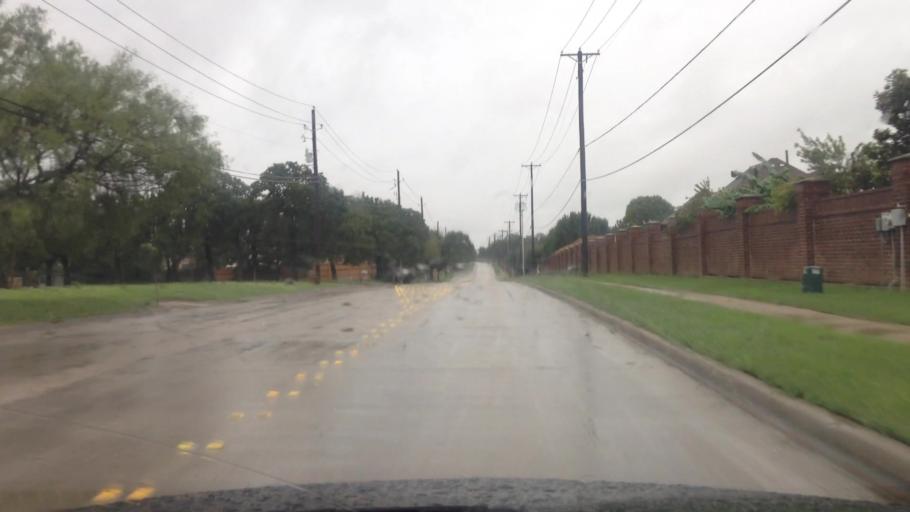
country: US
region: Texas
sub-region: Tarrant County
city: Keller
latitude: 32.9075
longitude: -97.2142
